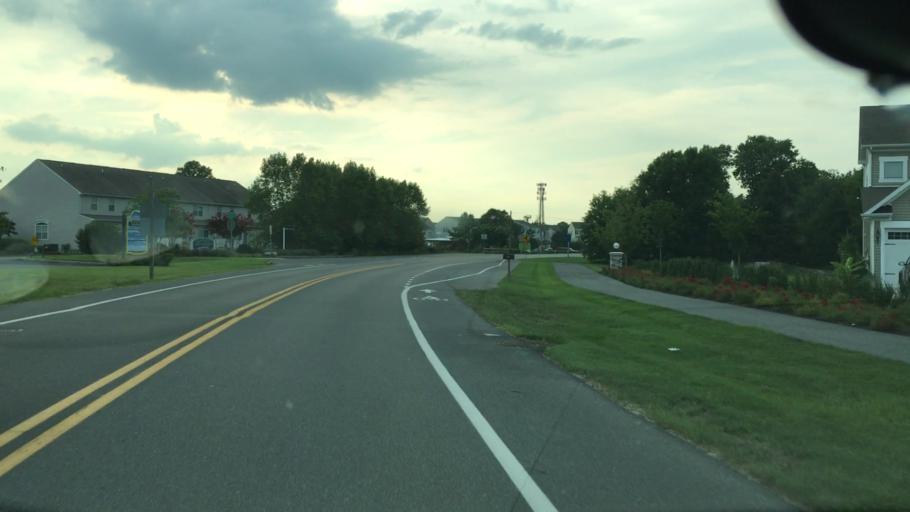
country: US
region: Delaware
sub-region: Sussex County
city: Ocean View
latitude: 38.5262
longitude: -75.0803
